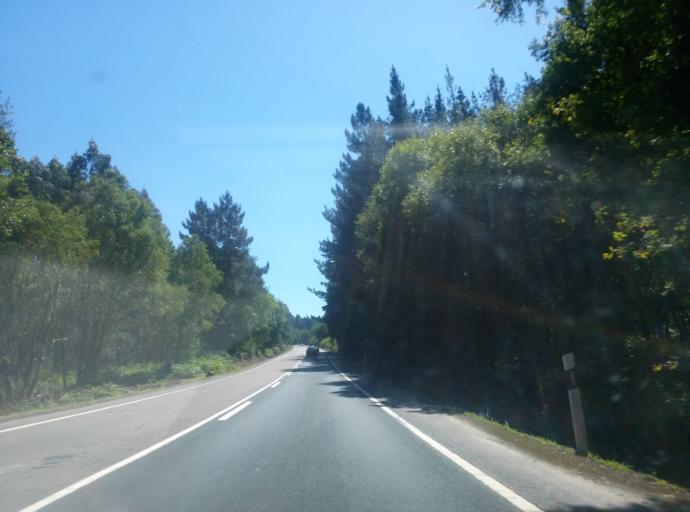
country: ES
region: Galicia
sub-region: Provincia de Lugo
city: Castro de Rei
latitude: 43.1410
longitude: -7.4023
